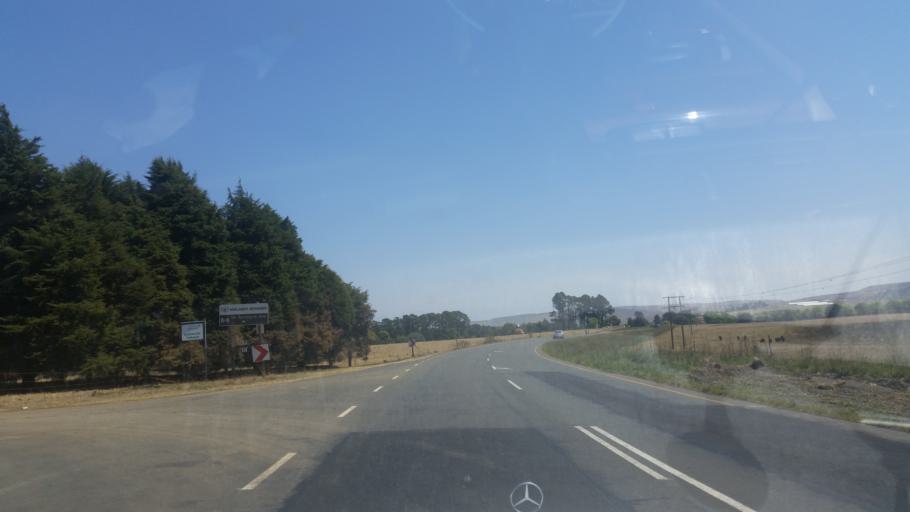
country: ZA
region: KwaZulu-Natal
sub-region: uMgungundlovu District Municipality
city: Mooirivier
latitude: -29.1495
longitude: 29.9839
